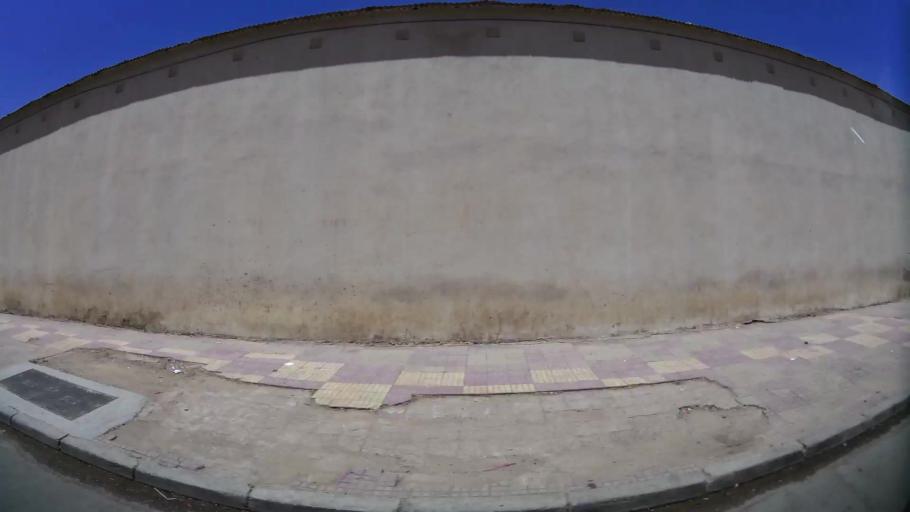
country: MA
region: Oriental
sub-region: Oujda-Angad
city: Oujda
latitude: 34.6743
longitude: -1.9286
